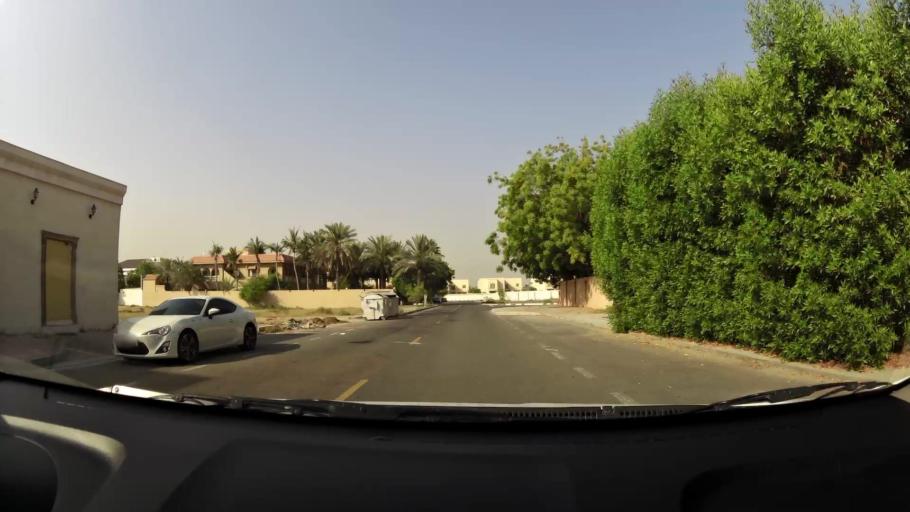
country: AE
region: Ash Shariqah
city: Sharjah
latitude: 25.3104
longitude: 55.3436
